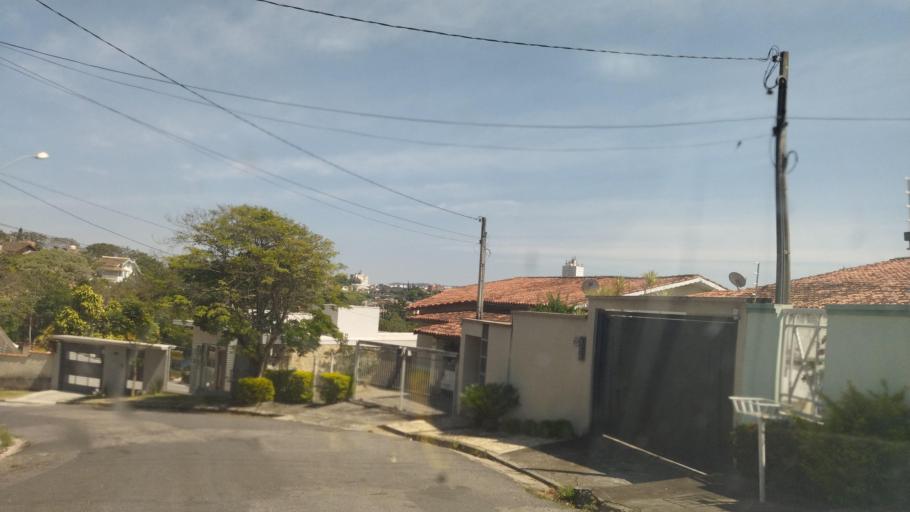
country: BR
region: Sao Paulo
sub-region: Atibaia
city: Atibaia
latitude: -23.1234
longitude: -46.5467
